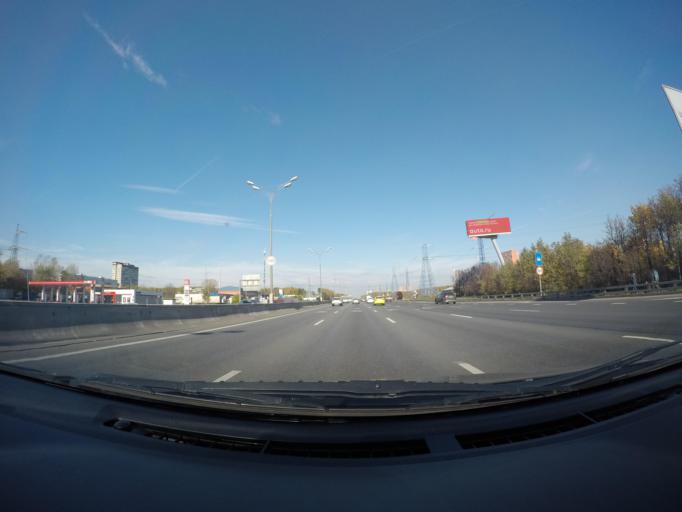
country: RU
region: Moscow
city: Ivanovskoye
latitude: 55.7797
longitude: 37.8425
